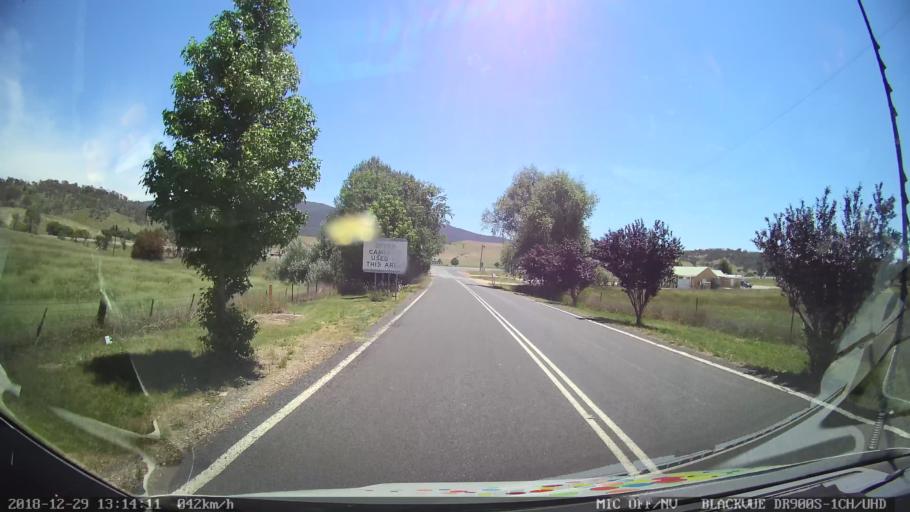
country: AU
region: Australian Capital Territory
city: Macarthur
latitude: -35.7040
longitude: 149.1599
